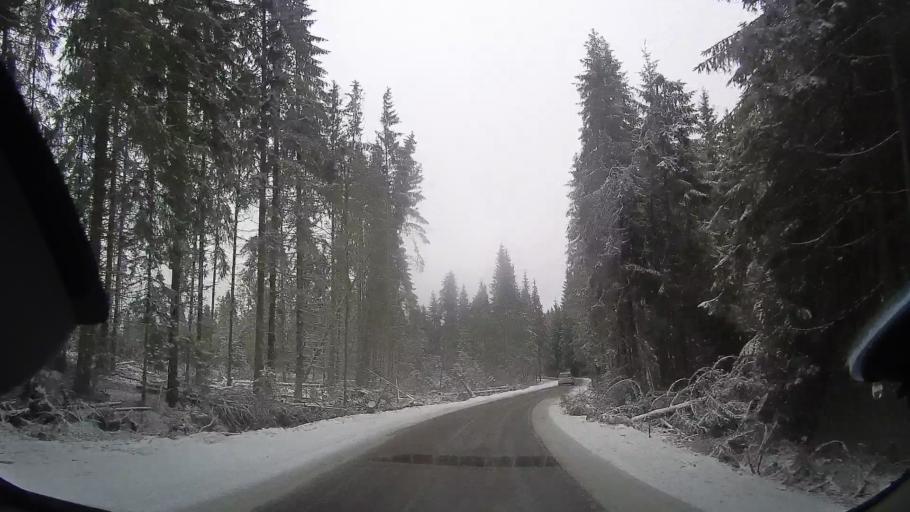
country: RO
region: Cluj
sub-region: Comuna Belis
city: Belis
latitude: 46.6497
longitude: 23.0411
